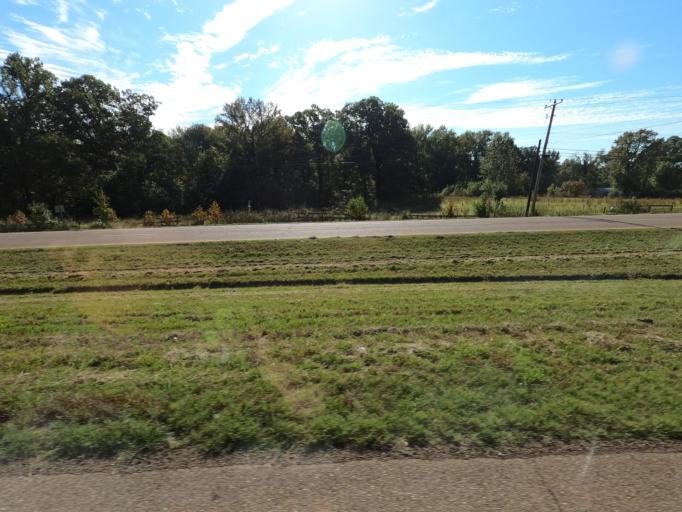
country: US
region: Tennessee
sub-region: Shelby County
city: Millington
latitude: 35.3862
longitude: -89.8597
